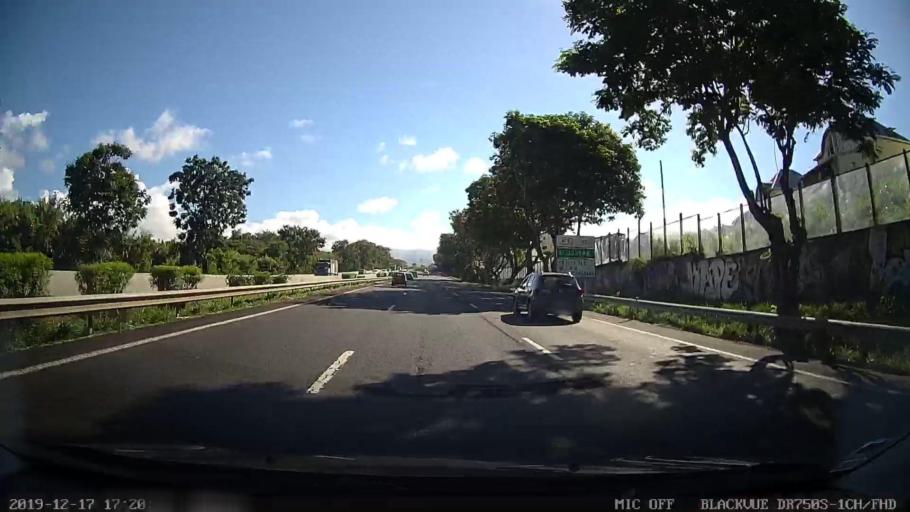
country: RE
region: Reunion
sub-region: Reunion
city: Saint-Pierre
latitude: -21.3319
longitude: 55.4659
